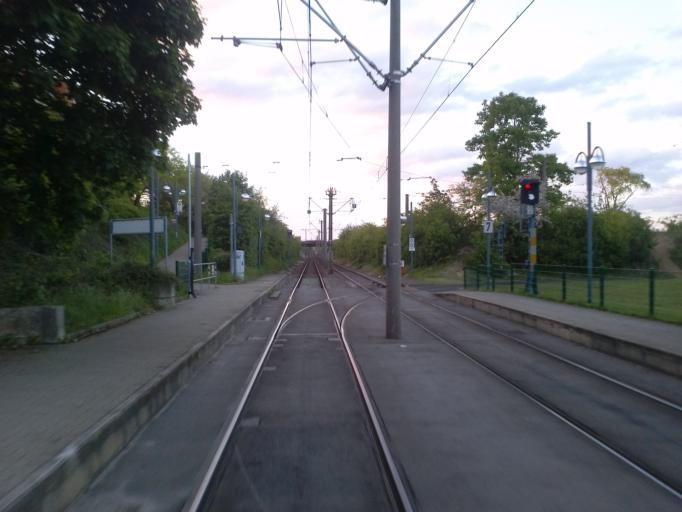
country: DE
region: Baden-Wuerttemberg
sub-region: Karlsruhe Region
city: Karlsruhe
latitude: 49.0340
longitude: 8.3766
